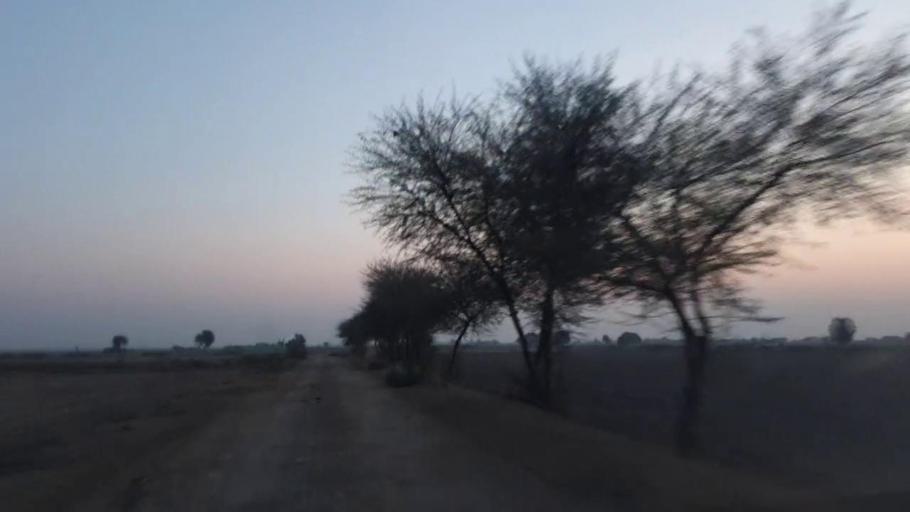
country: PK
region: Sindh
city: Naukot
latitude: 25.0190
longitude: 69.4117
